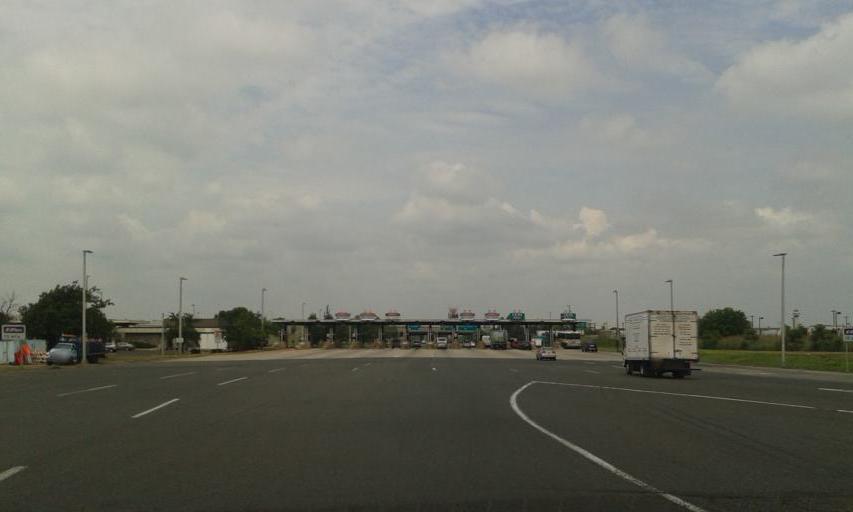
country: US
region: New Jersey
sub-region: Union County
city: Elizabeth
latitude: 40.6675
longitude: -74.1828
